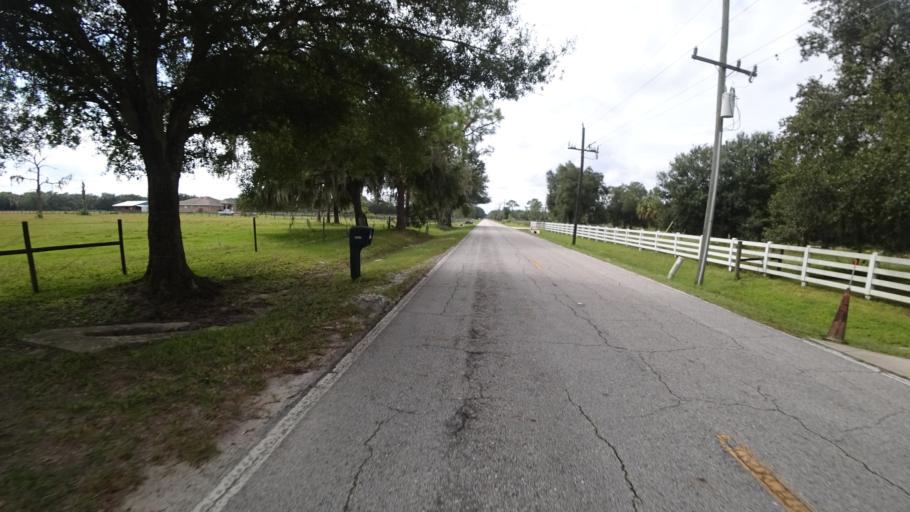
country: US
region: Florida
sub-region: Manatee County
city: Ellenton
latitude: 27.4878
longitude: -82.3825
